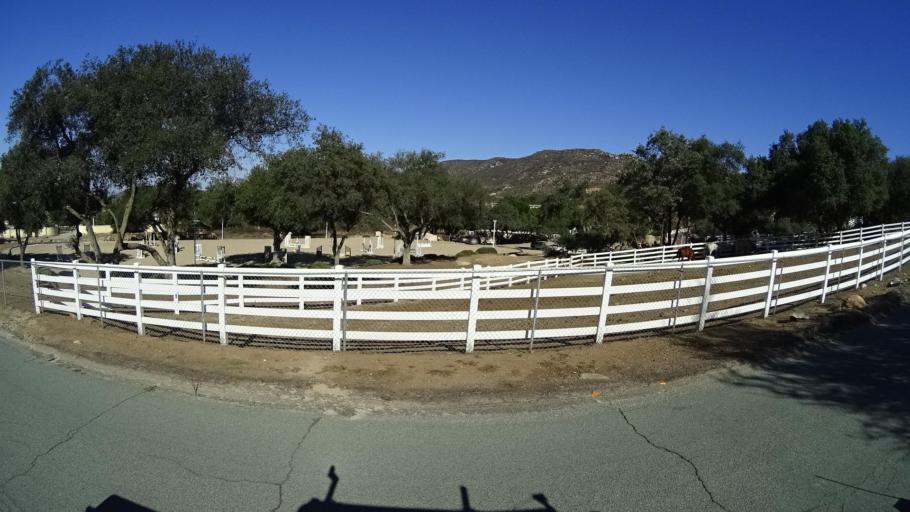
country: US
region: California
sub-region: San Diego County
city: Jamul
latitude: 32.7266
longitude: -116.8343
